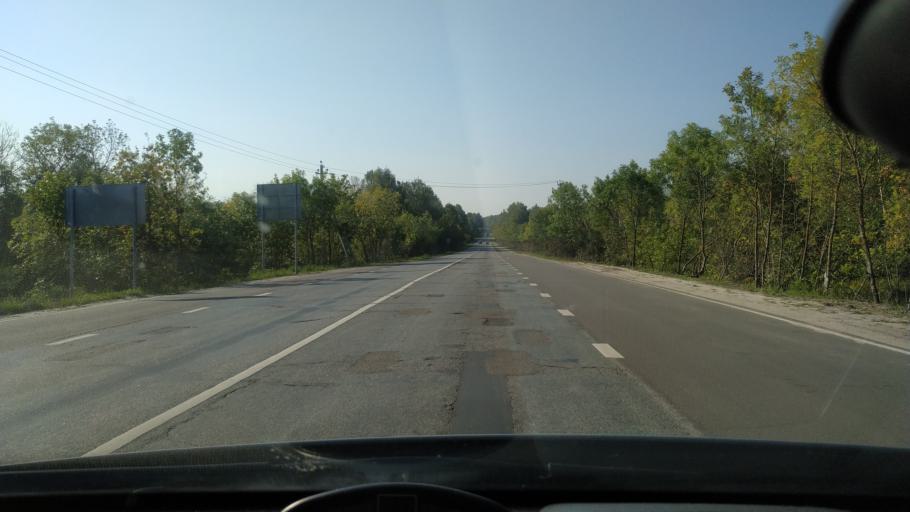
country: RU
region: Moskovskaya
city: Tugolesskiy Bor
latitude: 55.5501
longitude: 39.7036
